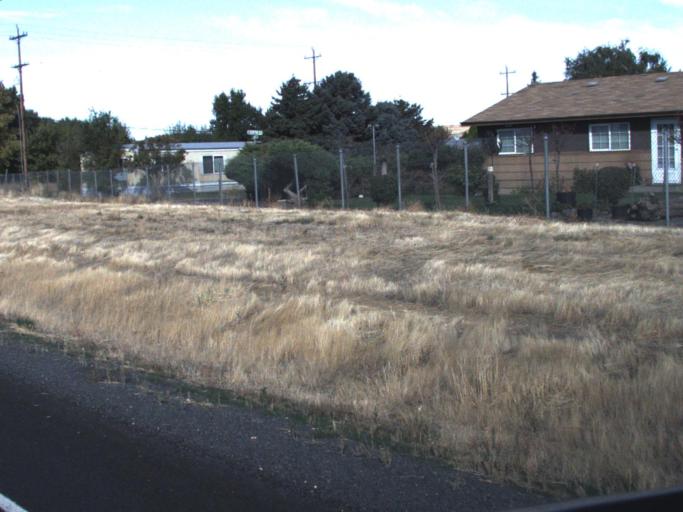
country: US
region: Washington
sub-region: Franklin County
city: Connell
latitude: 46.6524
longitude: -118.8674
